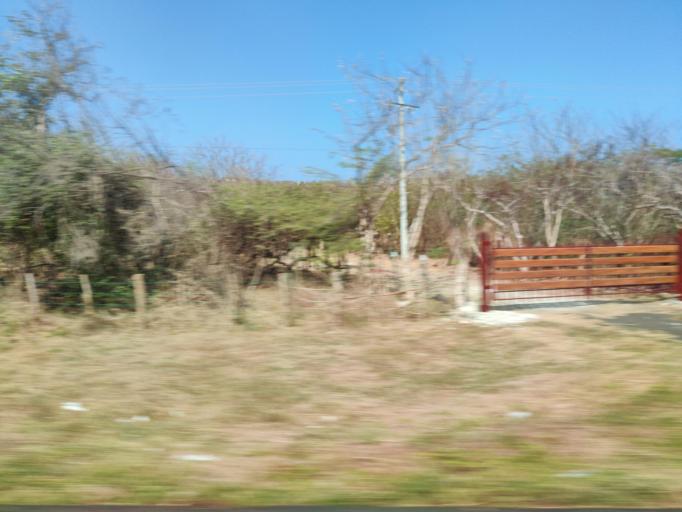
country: CO
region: Atlantico
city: Juan de Acosta
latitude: 10.8494
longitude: -75.1287
